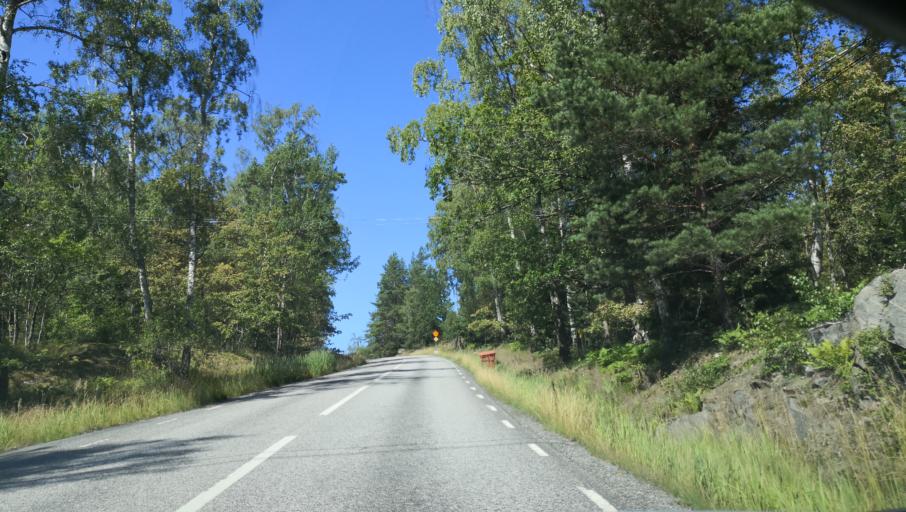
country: SE
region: Stockholm
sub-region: Varmdo Kommun
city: Mortnas
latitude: 59.3945
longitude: 18.4648
